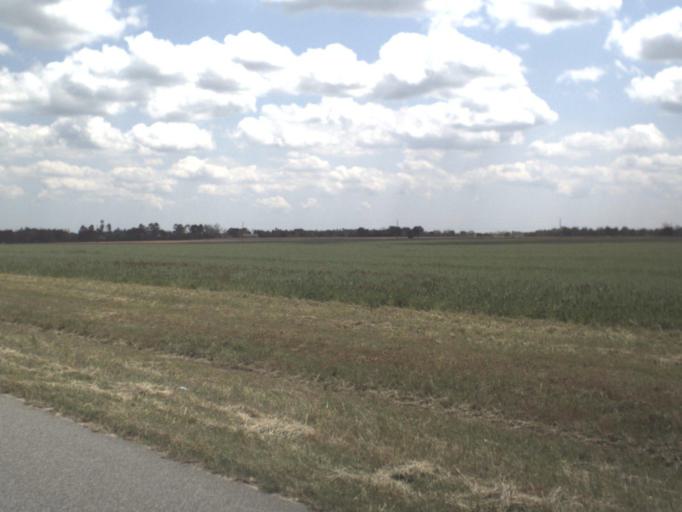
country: US
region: Florida
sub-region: Escambia County
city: Molino
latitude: 30.7363
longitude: -87.3549
